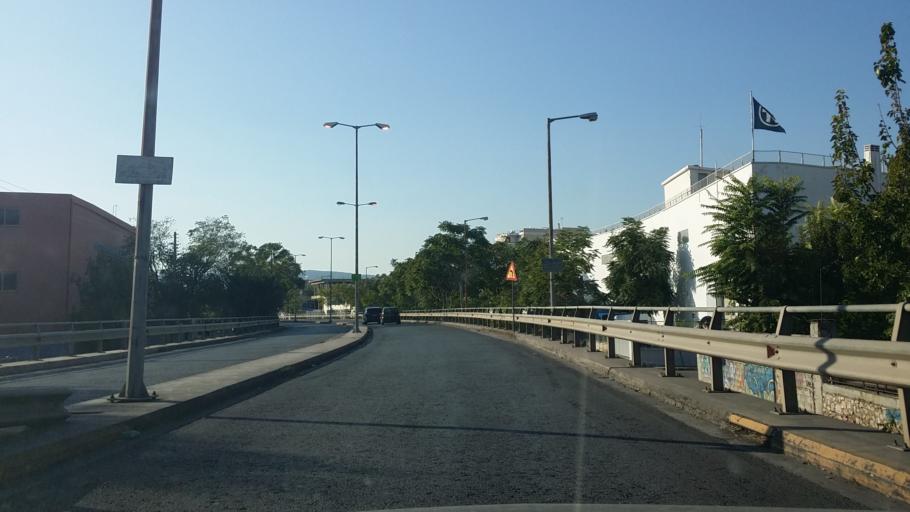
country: GR
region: Attica
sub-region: Nomarchia Athinas
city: Agioi Anargyroi
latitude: 38.0143
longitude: 23.7169
